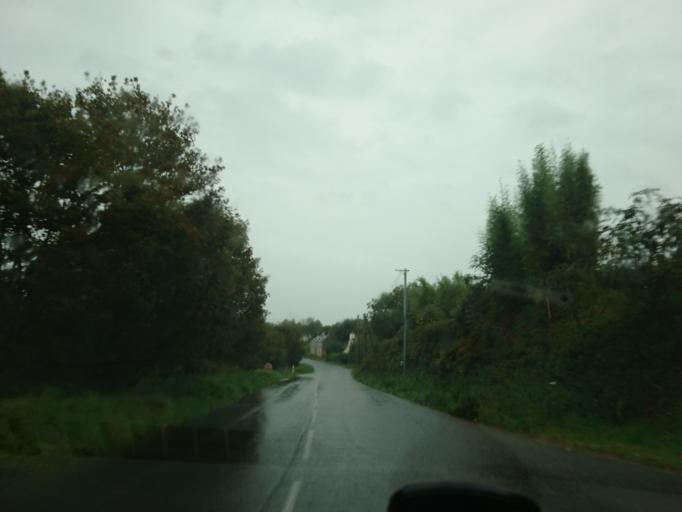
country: FR
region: Brittany
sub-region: Departement du Finistere
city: Plouguerneau
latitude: 48.5957
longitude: -4.5106
